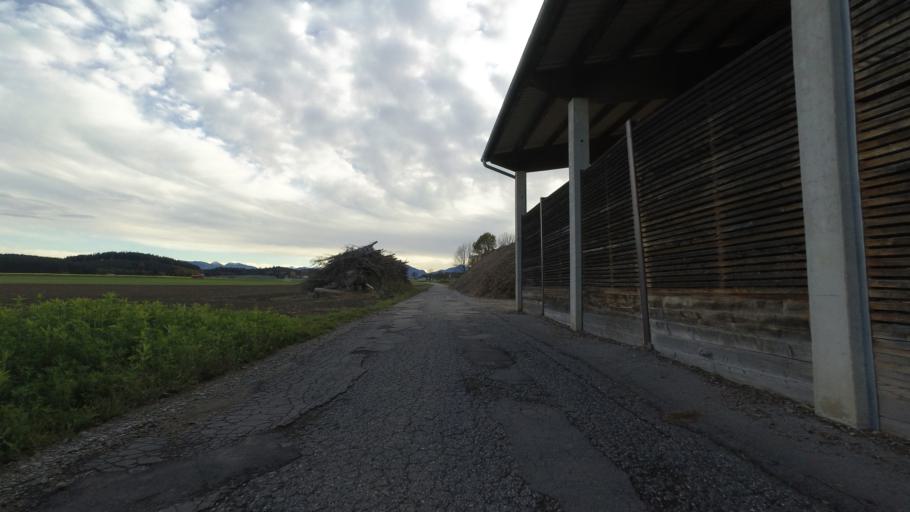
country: DE
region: Bavaria
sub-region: Upper Bavaria
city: Nussdorf
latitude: 47.9336
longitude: 12.5923
